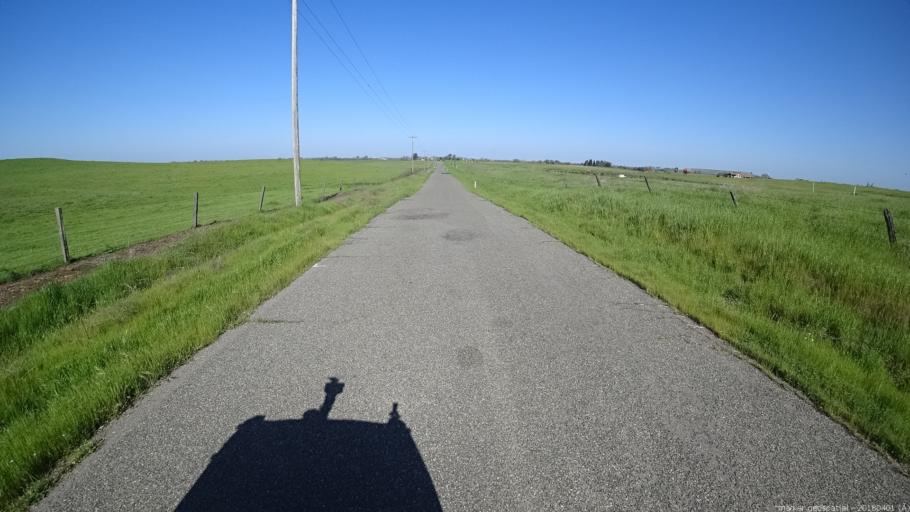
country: US
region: California
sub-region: Sacramento County
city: Rancho Murieta
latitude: 38.4771
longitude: -121.1759
